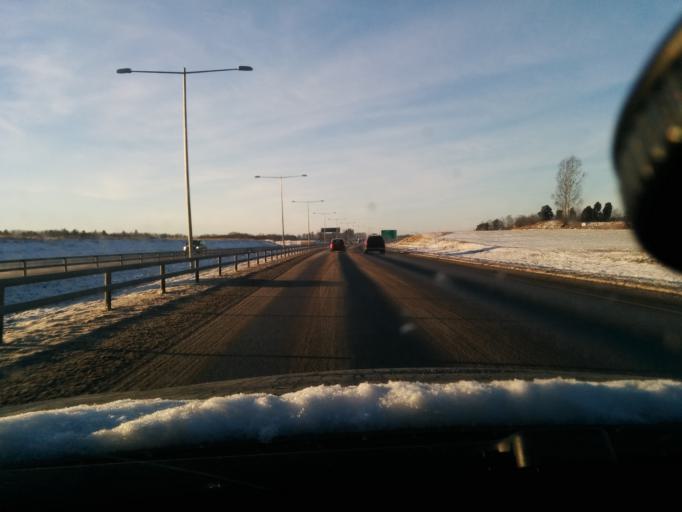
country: SE
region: Stockholm
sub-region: Taby Kommun
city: Taby
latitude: 59.4749
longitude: 18.0403
